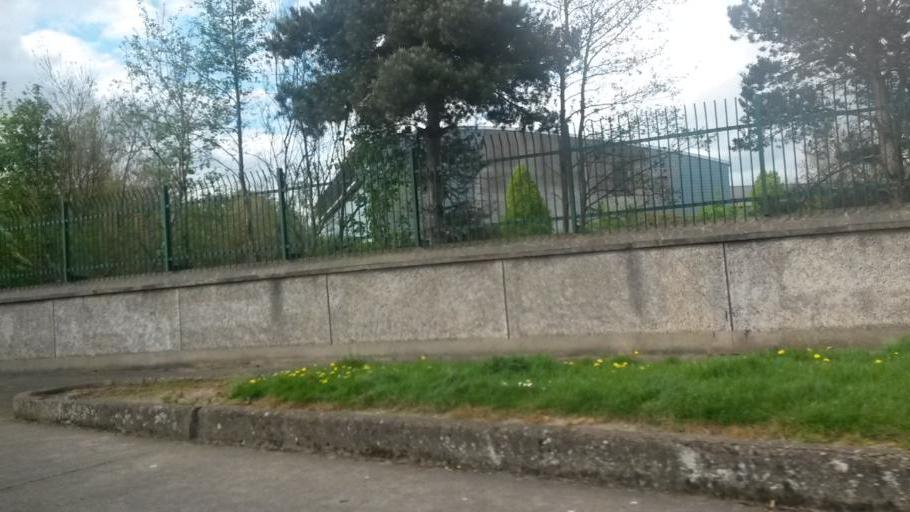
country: IE
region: Leinster
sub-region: Dublin City
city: Finglas
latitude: 53.3882
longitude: -6.2876
